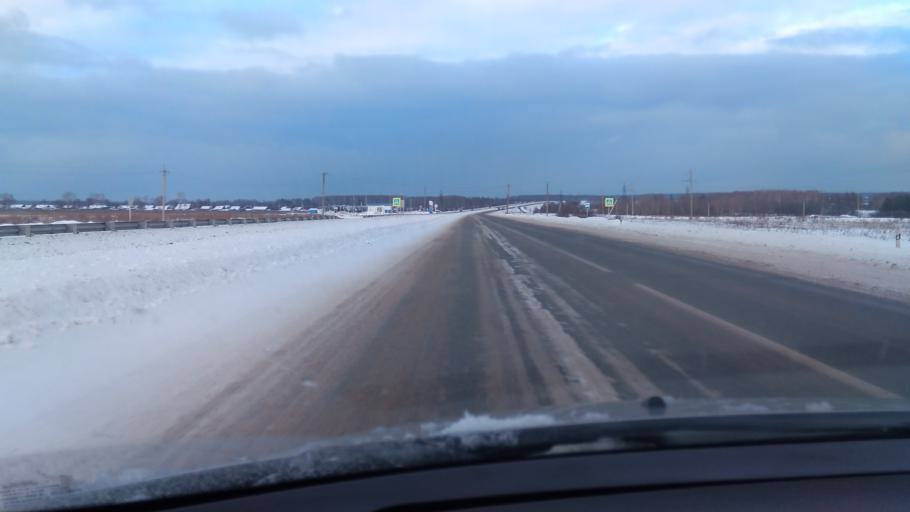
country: RU
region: Sverdlovsk
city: Tsementnyy
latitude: 57.4932
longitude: 60.1768
